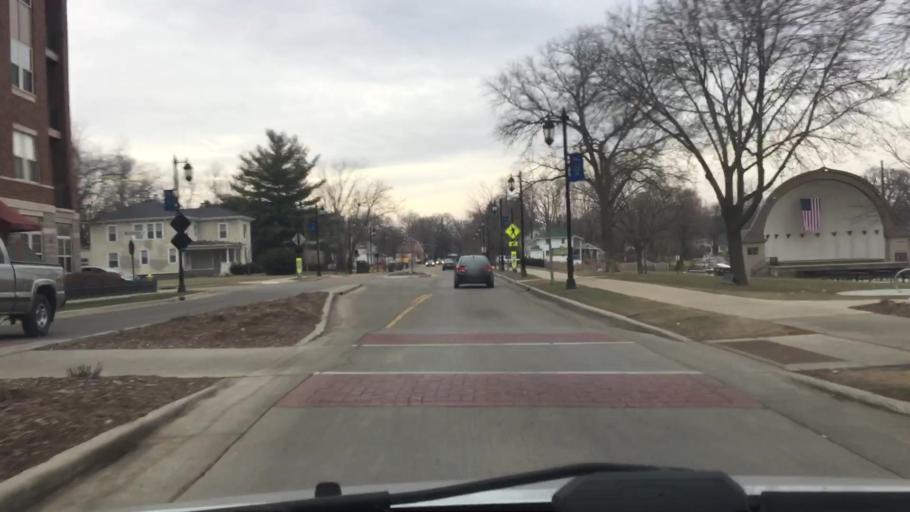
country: US
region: Wisconsin
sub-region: Waukesha County
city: Oconomowoc
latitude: 43.1120
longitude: -88.5021
